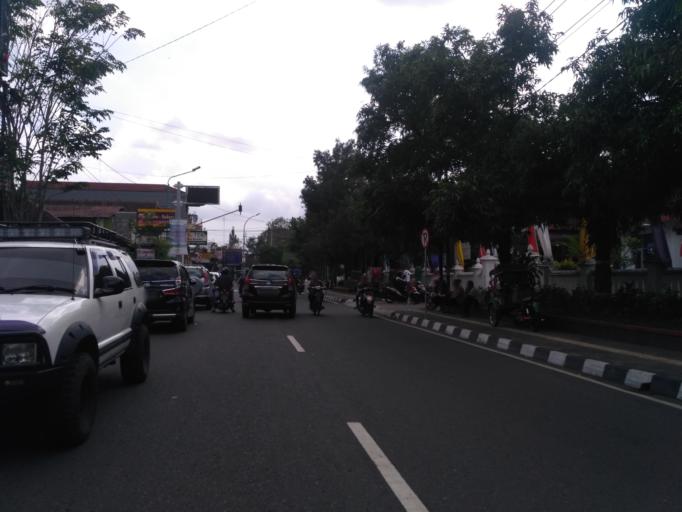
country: ID
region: Daerah Istimewa Yogyakarta
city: Sleman
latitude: -7.7195
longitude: 110.3548
